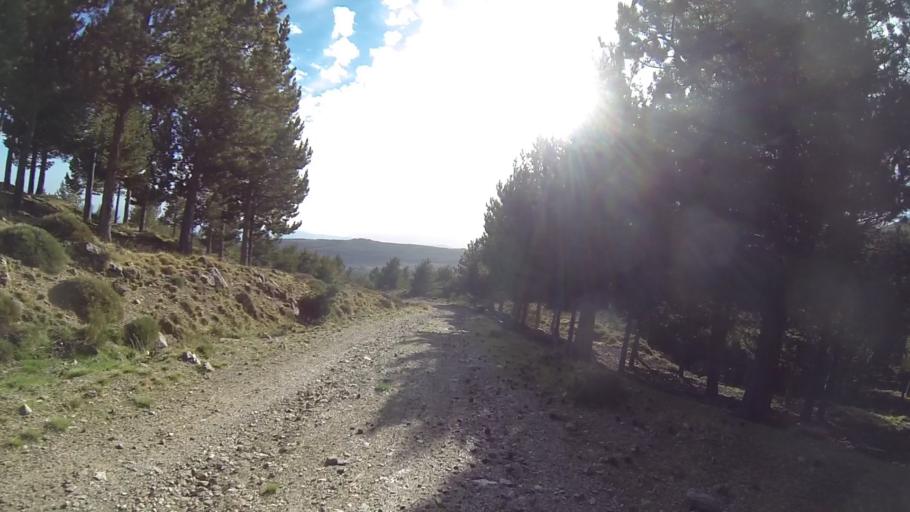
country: ES
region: Andalusia
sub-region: Provincia de Almeria
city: Paterna del Rio
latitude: 37.0791
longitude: -2.9040
